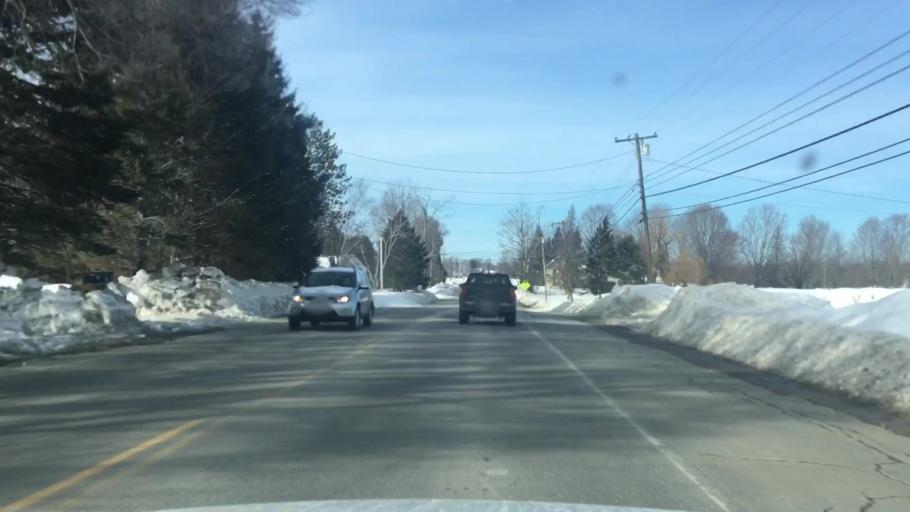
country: US
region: Maine
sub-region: Penobscot County
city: Charleston
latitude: 45.0136
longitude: -69.0270
